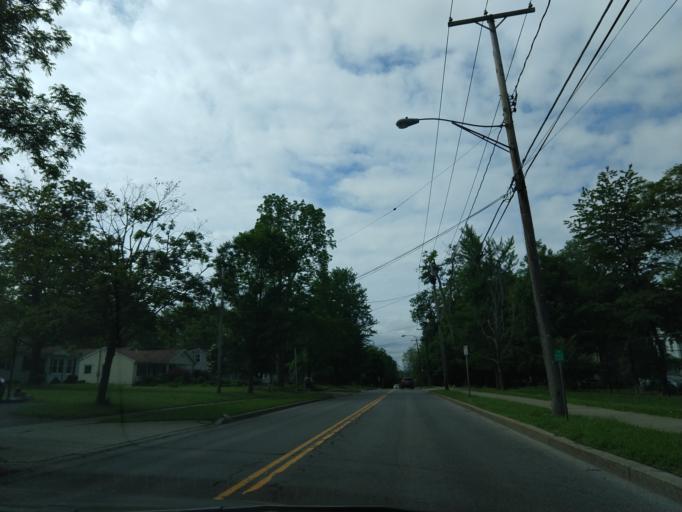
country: US
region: New York
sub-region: Erie County
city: East Aurora
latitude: 42.7613
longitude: -78.6080
